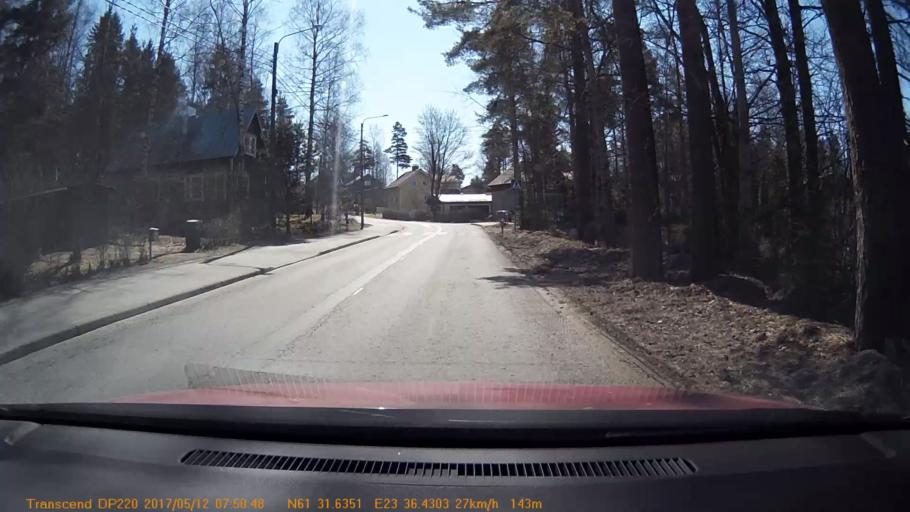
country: FI
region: Pirkanmaa
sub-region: Tampere
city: Yloejaervi
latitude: 61.5274
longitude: 23.6071
